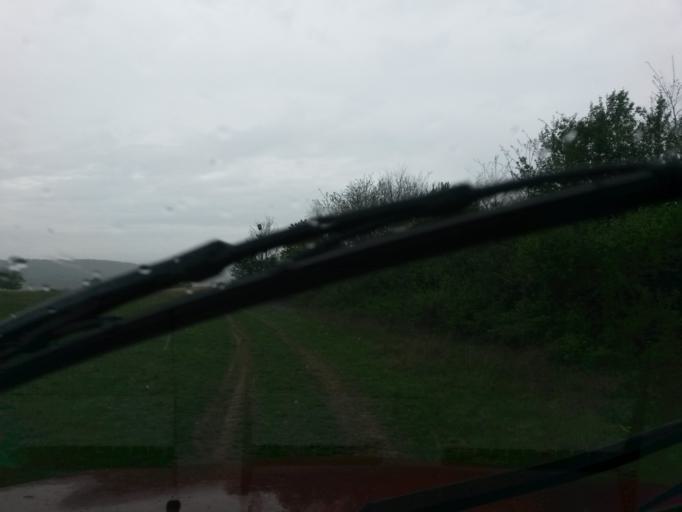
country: HU
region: Borsod-Abauj-Zemplen
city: Gonc
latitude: 48.5128
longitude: 21.3403
